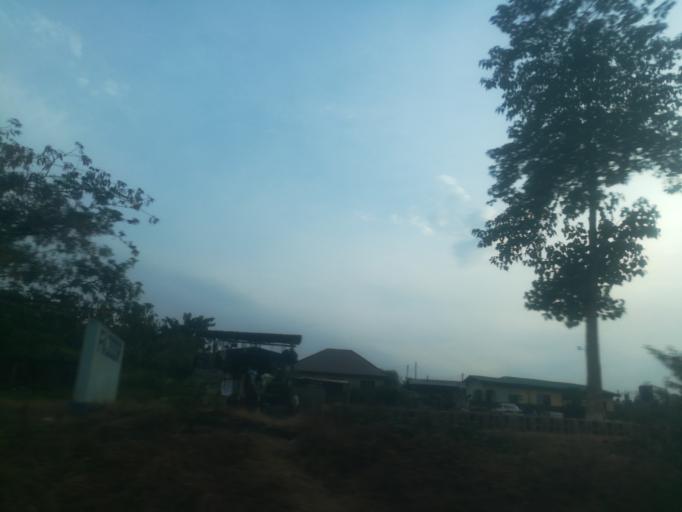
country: NG
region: Ogun
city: Abeokuta
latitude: 7.1400
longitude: 3.2727
